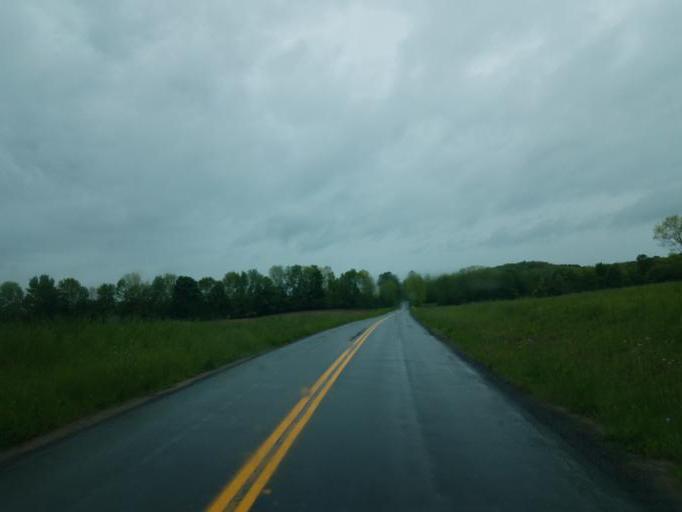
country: US
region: New York
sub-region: Herkimer County
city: Frankfort
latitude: 42.9250
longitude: -75.1295
